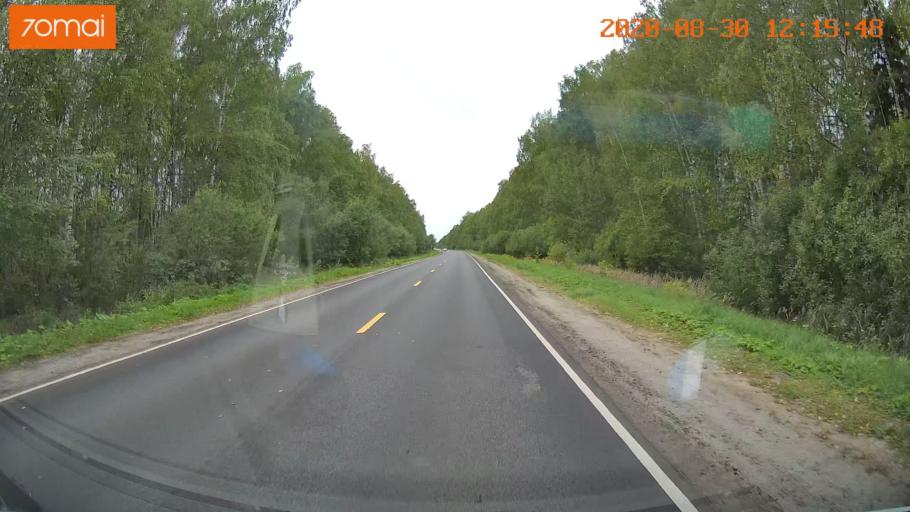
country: RU
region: Ivanovo
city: Yur'yevets
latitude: 57.3185
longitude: 43.0206
